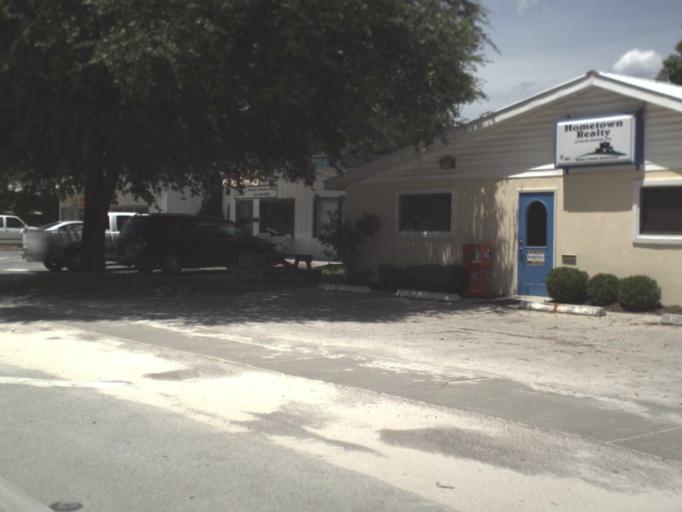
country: US
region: Florida
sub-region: Gilchrist County
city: Trenton
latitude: 29.7548
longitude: -82.8623
